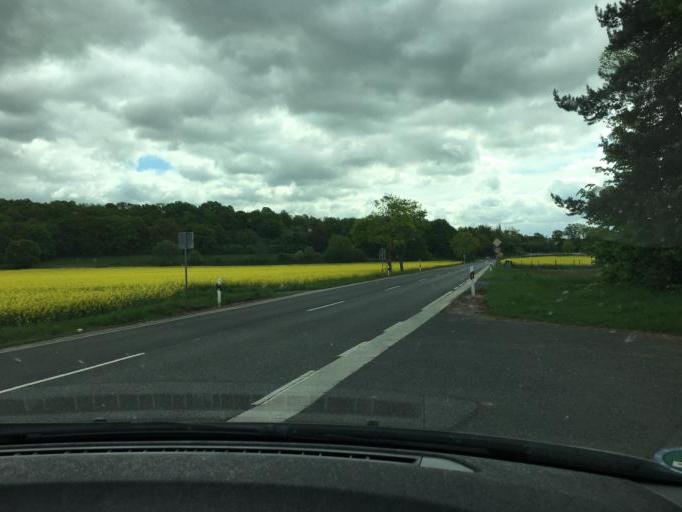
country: DE
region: North Rhine-Westphalia
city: Zulpich
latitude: 50.6447
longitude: 6.6513
